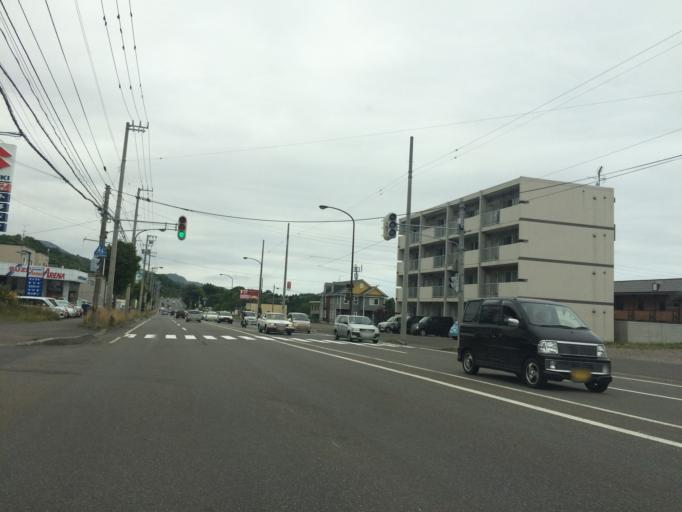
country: JP
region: Hokkaido
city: Otaru
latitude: 43.1439
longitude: 141.1452
